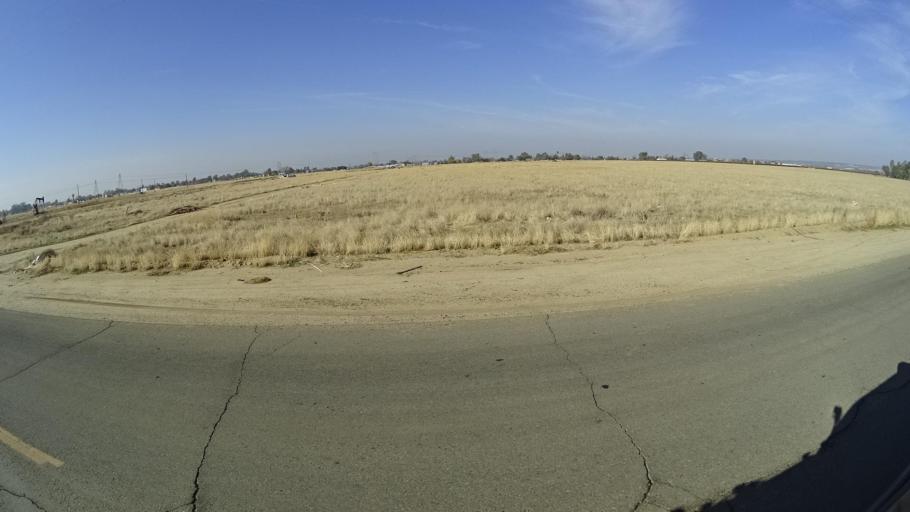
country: US
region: California
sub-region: Kern County
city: Lamont
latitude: 35.3438
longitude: -118.8964
